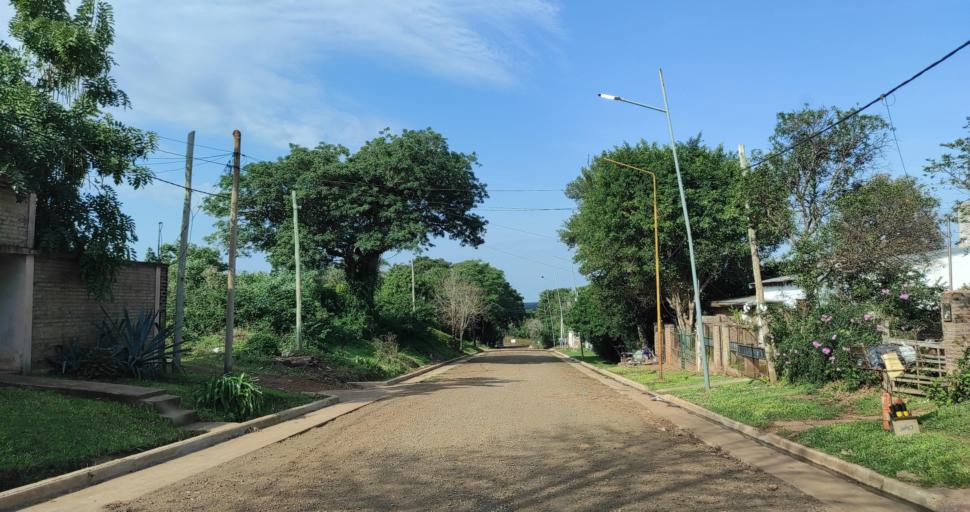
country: AR
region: Corrientes
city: Santo Tome
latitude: -28.5524
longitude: -56.0299
